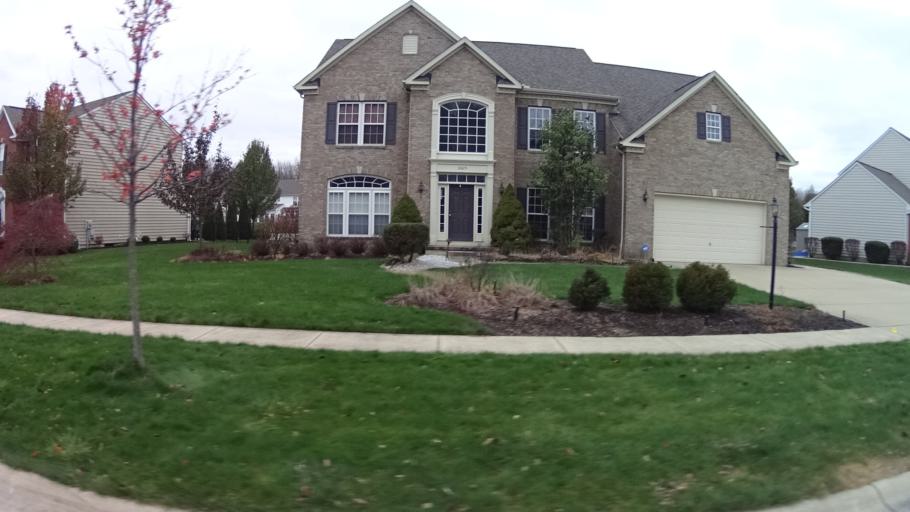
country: US
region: Ohio
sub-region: Cuyahoga County
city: Bay Village
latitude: 41.4831
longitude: -81.9734
